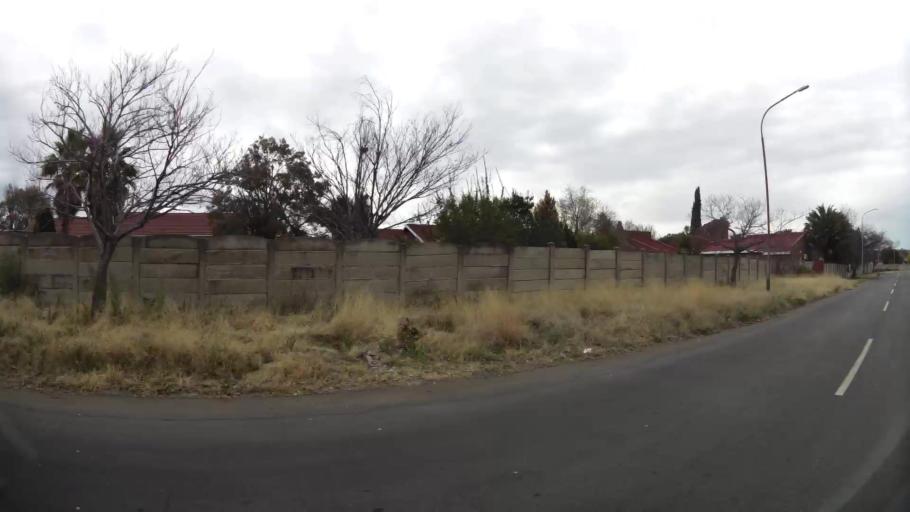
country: ZA
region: Orange Free State
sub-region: Fezile Dabi District Municipality
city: Kroonstad
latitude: -27.6320
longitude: 27.2420
